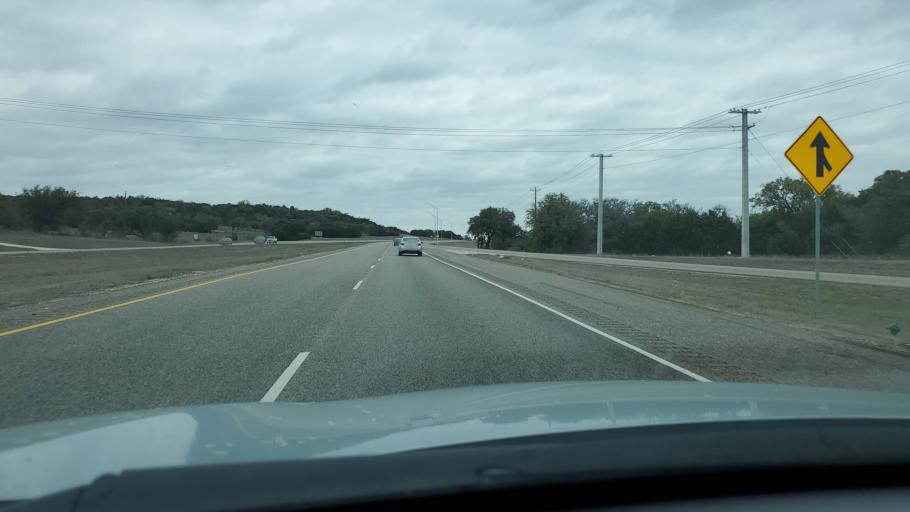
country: US
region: Texas
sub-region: Williamson County
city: Florence
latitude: 30.8819
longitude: -97.8003
